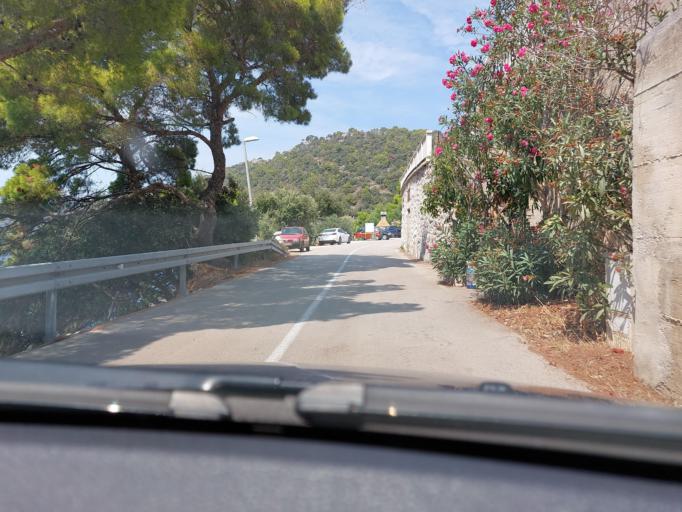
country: HR
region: Dubrovacko-Neretvanska
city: Smokvica
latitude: 42.7478
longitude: 16.8259
